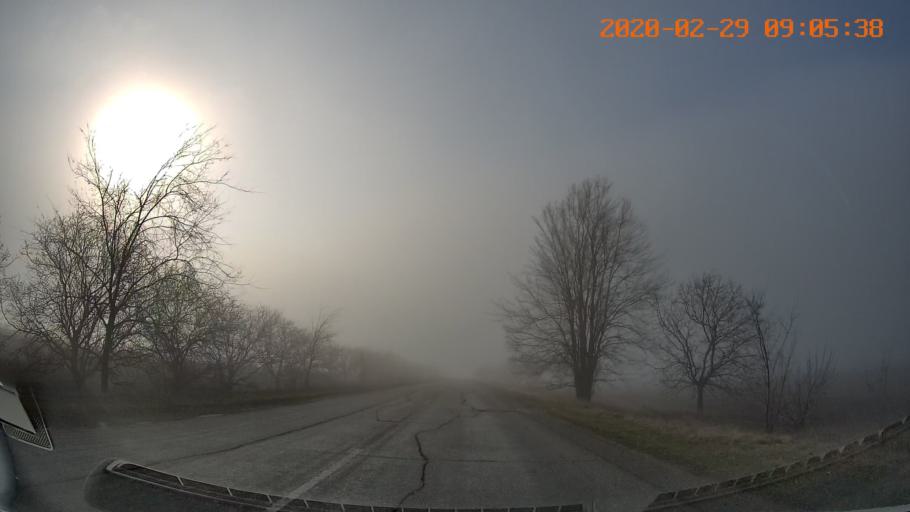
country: MD
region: Telenesti
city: Tiraspolul Nou
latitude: 46.8866
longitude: 29.7411
